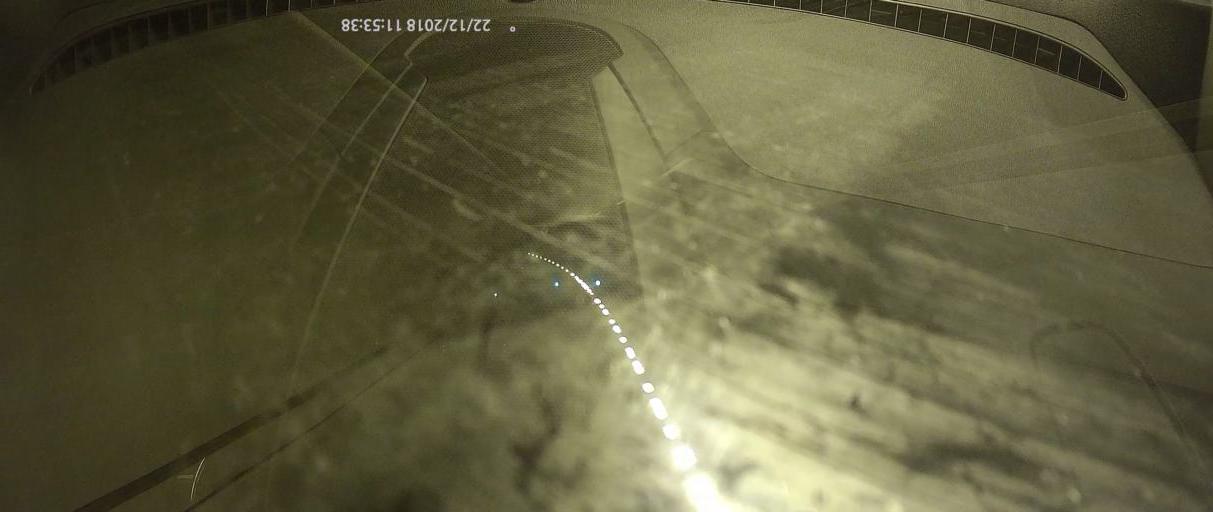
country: BG
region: Pernik
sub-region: Obshtina Pernik
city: Pernik
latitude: 42.6260
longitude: 23.1299
